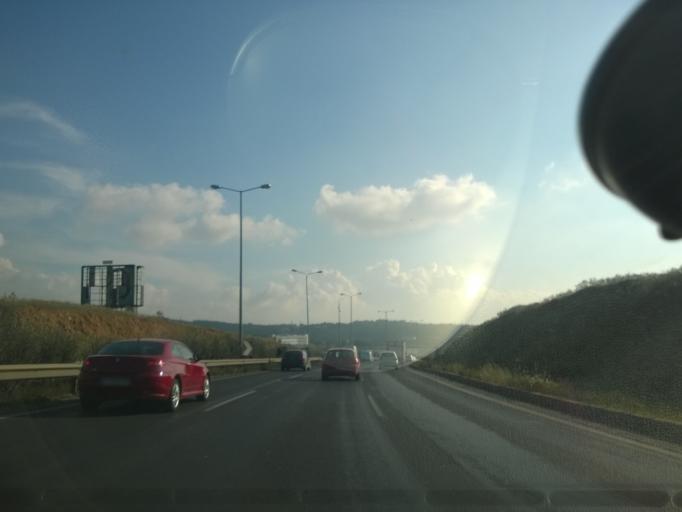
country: GR
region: Central Macedonia
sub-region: Nomos Thessalonikis
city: Pylaia
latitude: 40.6109
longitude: 22.9998
